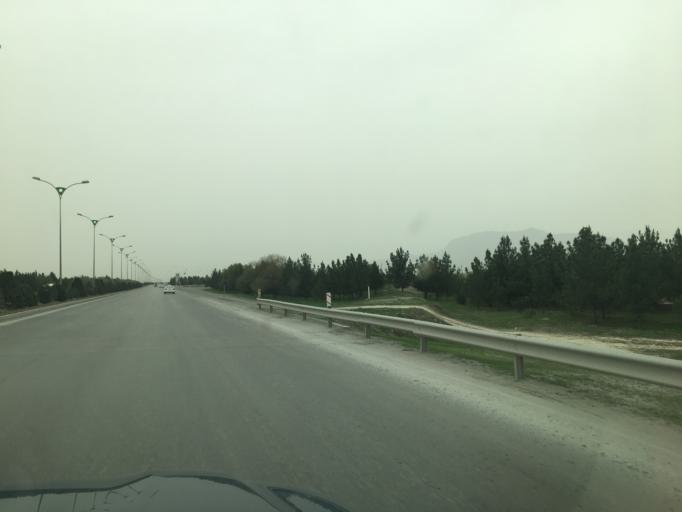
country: TM
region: Ahal
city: Abadan
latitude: 38.1470
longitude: 57.9883
